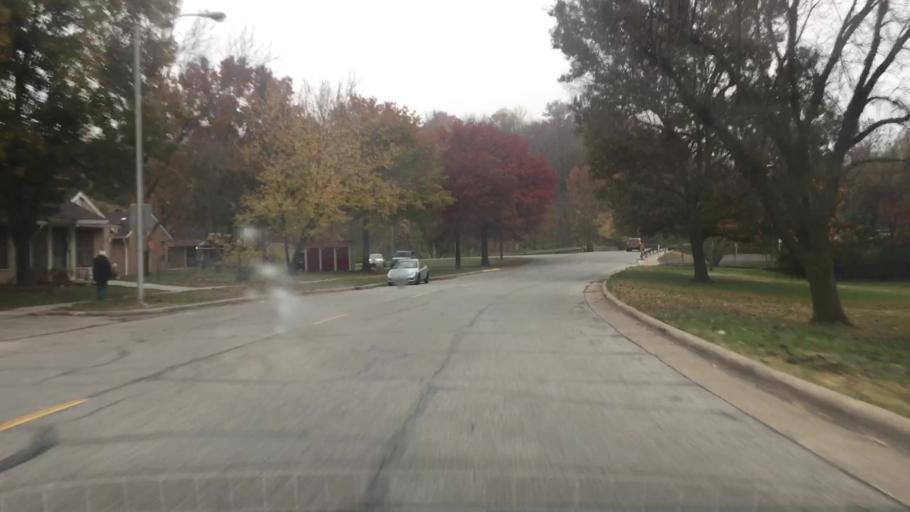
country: US
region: Missouri
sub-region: Callaway County
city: Fulton
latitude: 38.8447
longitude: -91.9540
